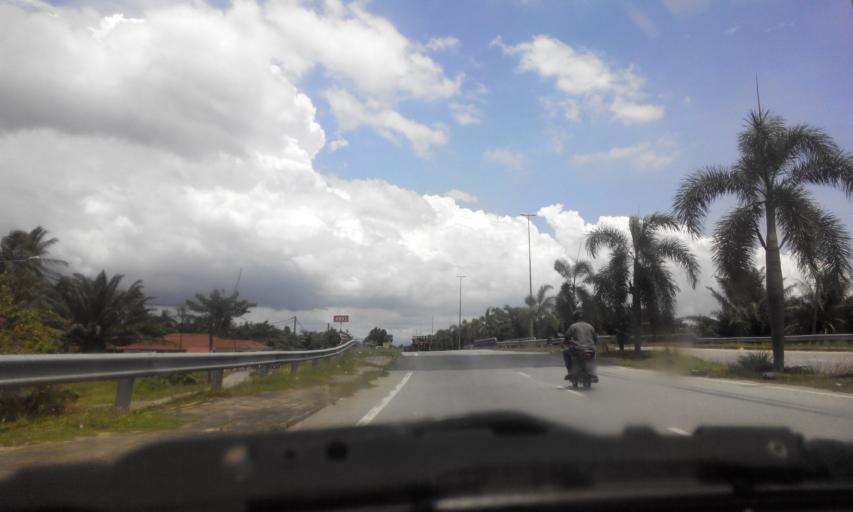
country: MY
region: Perak
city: Parit Buntar
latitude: 5.1194
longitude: 100.5219
